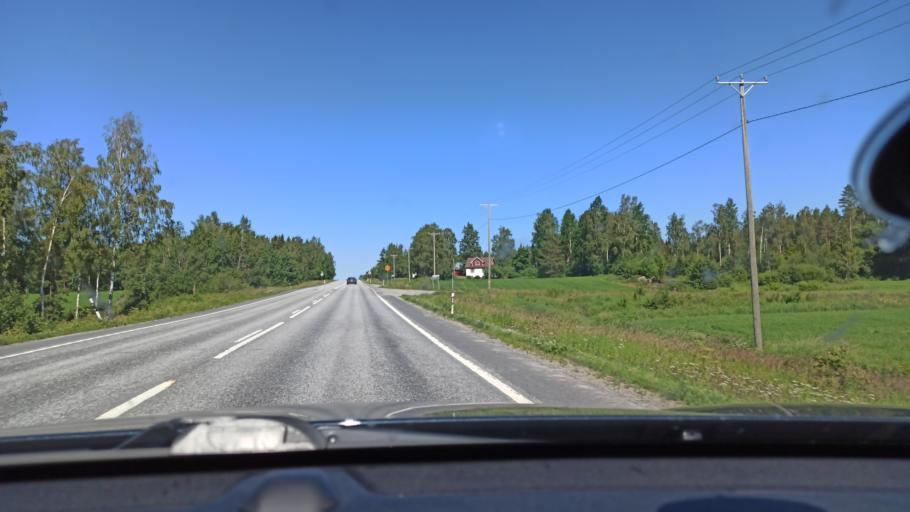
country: FI
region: Ostrobothnia
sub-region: Vaasa
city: Voera
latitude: 63.2402
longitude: 22.2613
